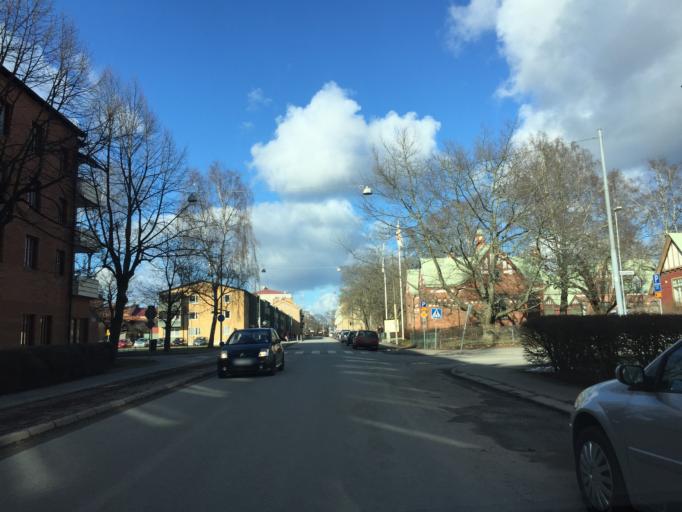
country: SE
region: OErebro
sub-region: Orebro Kommun
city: Orebro
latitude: 59.2790
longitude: 15.2222
